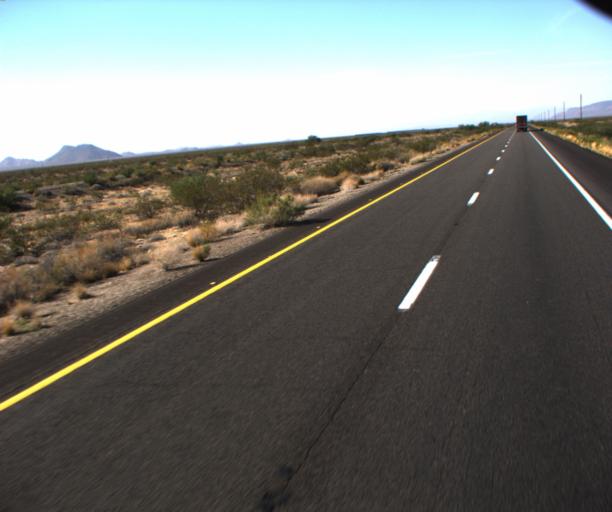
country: US
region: Arizona
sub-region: Mohave County
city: Kingman
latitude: 35.0067
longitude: -114.1358
